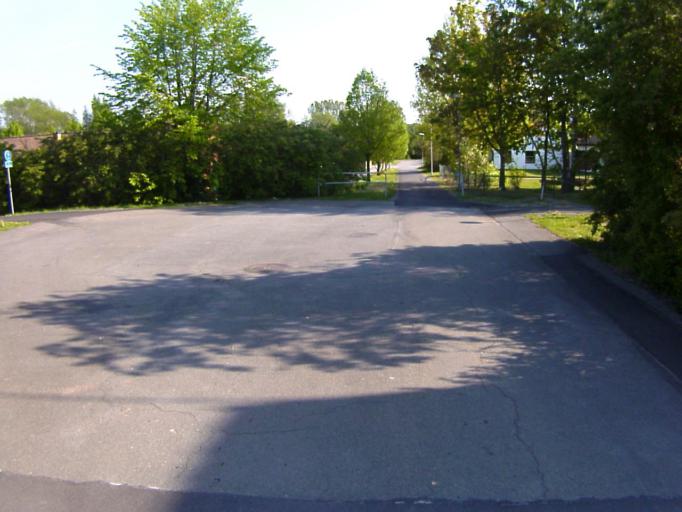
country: SE
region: Skane
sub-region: Kristianstads Kommun
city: Onnestad
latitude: 56.0549
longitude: 14.0258
